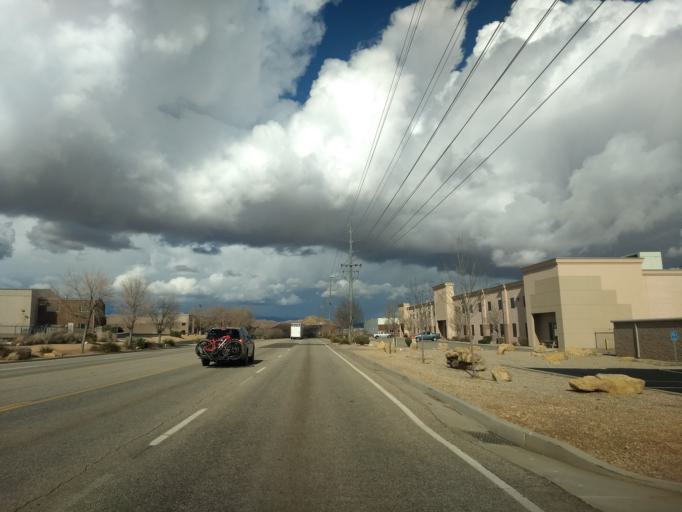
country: US
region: Utah
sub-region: Washington County
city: Saint George
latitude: 37.0366
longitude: -113.5592
